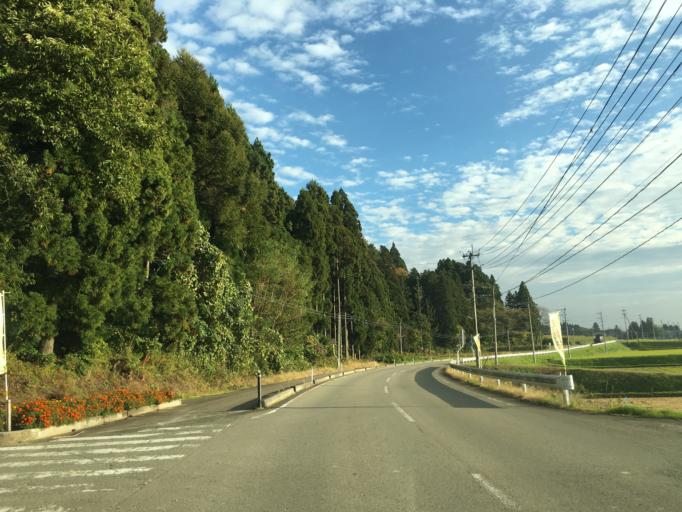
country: JP
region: Fukushima
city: Inawashiro
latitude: 37.5543
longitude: 140.1403
